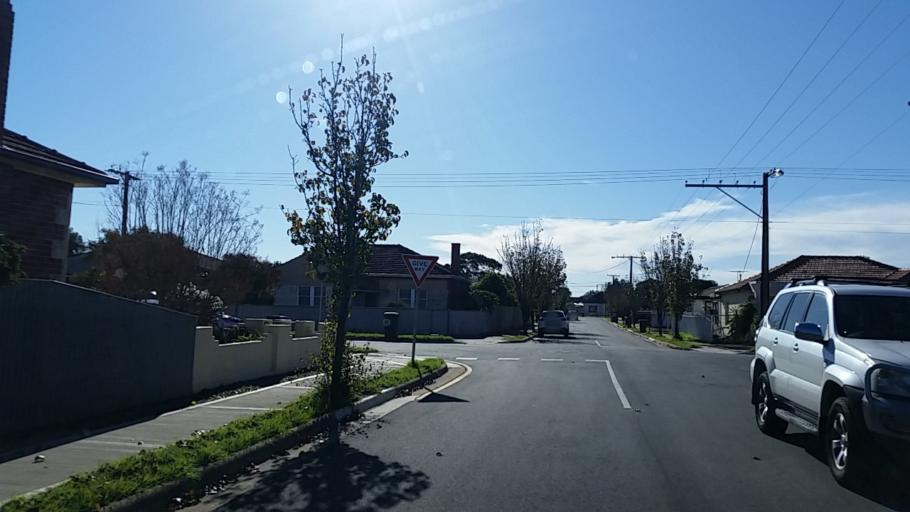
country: AU
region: South Australia
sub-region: Charles Sturt
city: Woodville West
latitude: -34.8851
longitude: 138.5272
